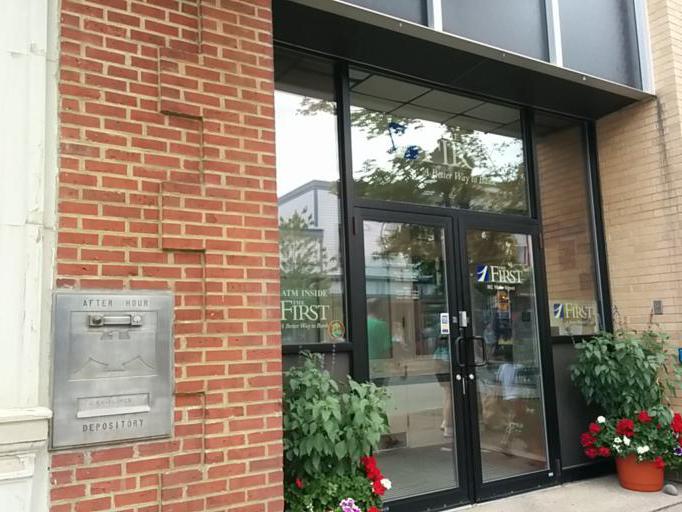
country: US
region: Maine
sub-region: Hancock County
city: Bar Harbor
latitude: 44.3892
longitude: -68.2046
